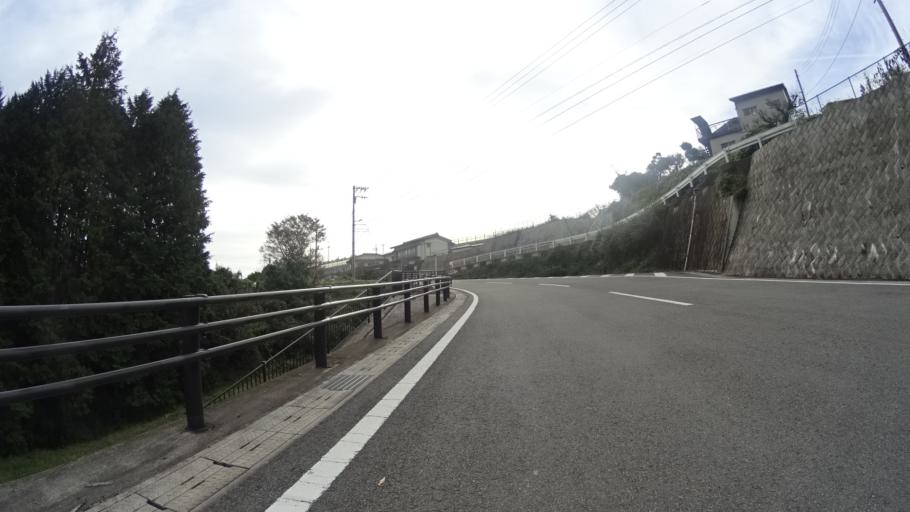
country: JP
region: Yamanashi
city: Uenohara
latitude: 35.6346
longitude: 139.0606
